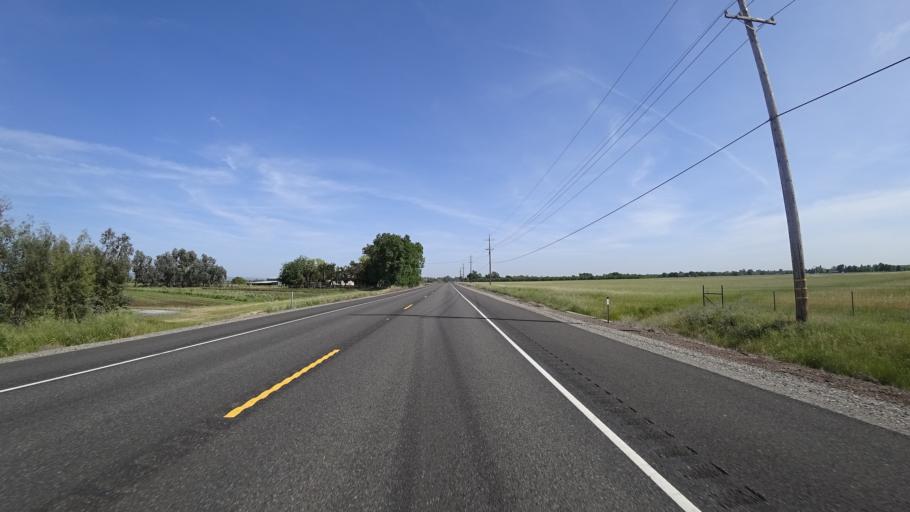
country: US
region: California
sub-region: Glenn County
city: Hamilton City
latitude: 39.8306
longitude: -121.9317
